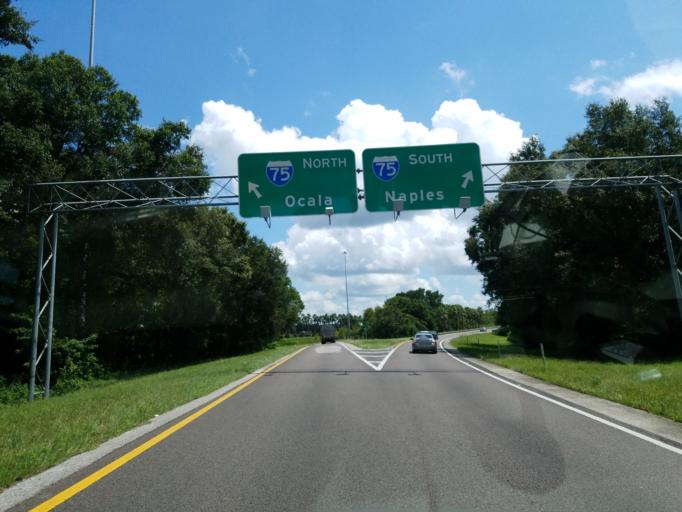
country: US
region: Florida
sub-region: Hillsborough County
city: Mango
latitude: 28.0002
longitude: -82.3299
